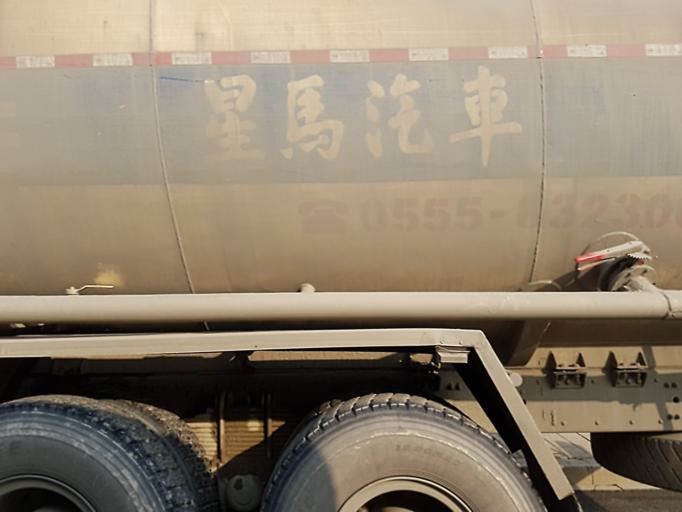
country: CN
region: Zhejiang Sheng
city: Jiangcun
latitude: 30.2962
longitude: 120.0413
